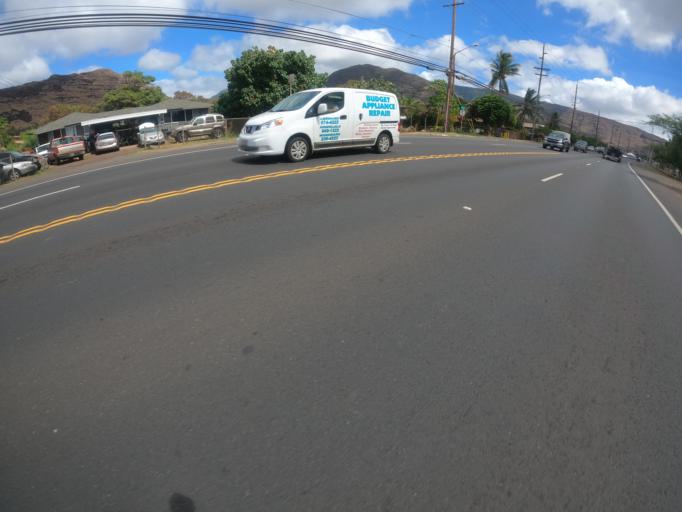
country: US
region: Hawaii
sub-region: Honolulu County
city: Nanakuli
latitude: 21.3956
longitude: -158.1617
